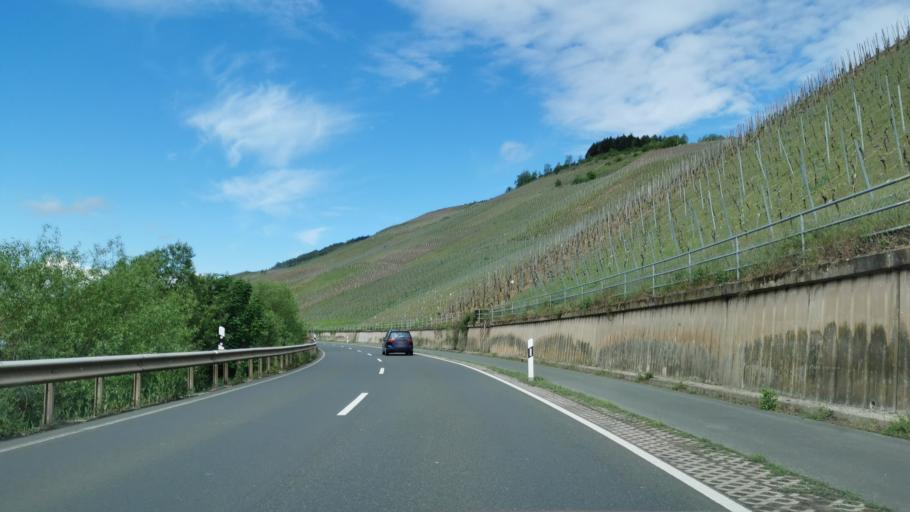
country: DE
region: Rheinland-Pfalz
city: Enkirch
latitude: 49.9841
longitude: 7.1005
